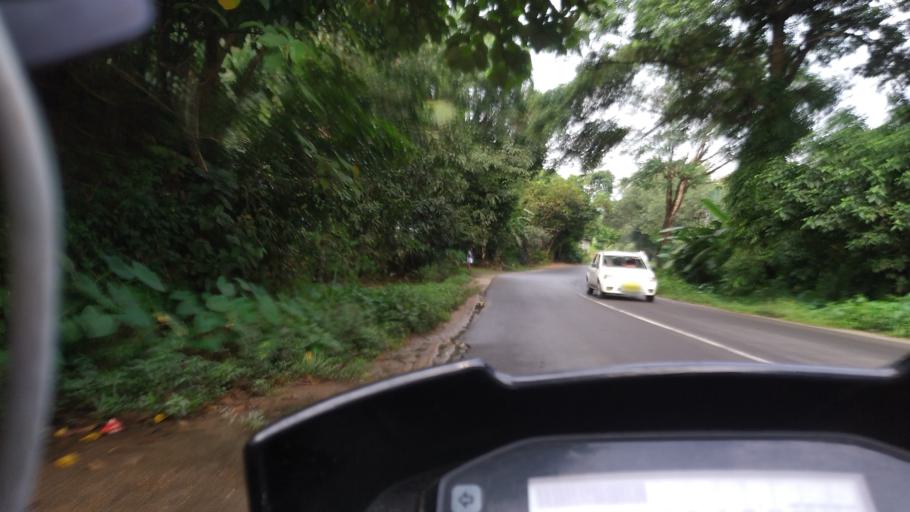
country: IN
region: Kerala
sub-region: Idukki
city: Kuttampuzha
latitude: 10.0500
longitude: 76.7266
